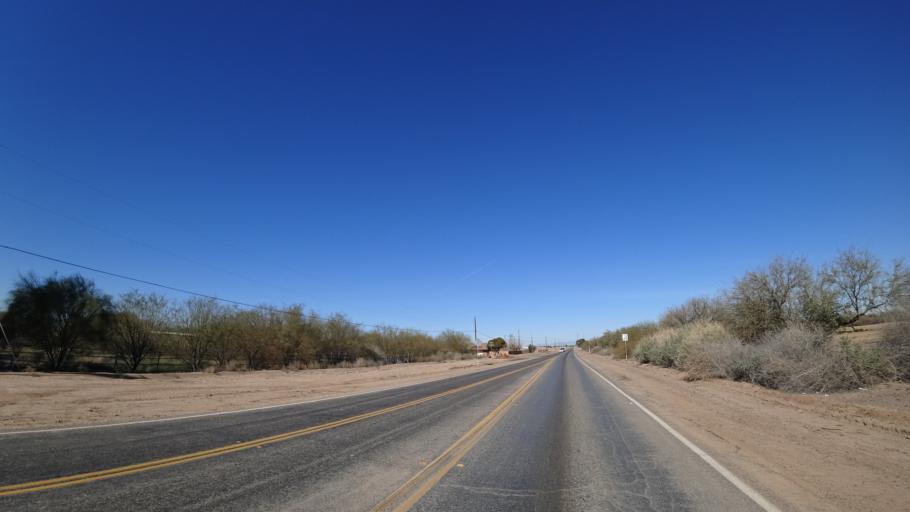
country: US
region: Arizona
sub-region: Maricopa County
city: Avondale
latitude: 33.3927
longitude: -112.3233
